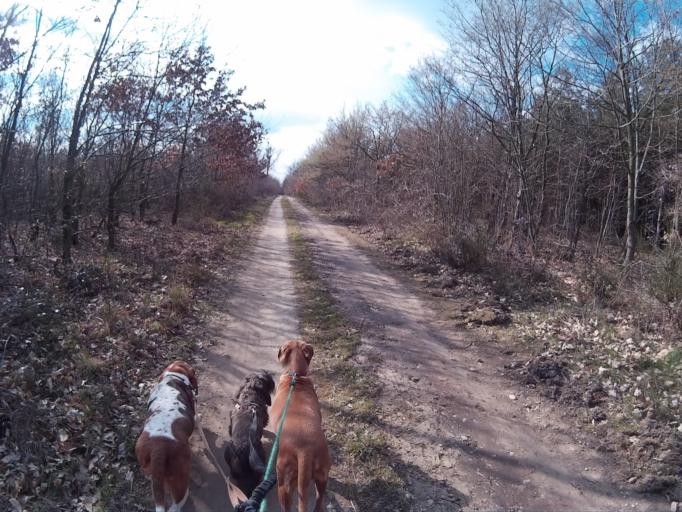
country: HU
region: Vas
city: Sarvar
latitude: 47.1993
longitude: 16.9915
